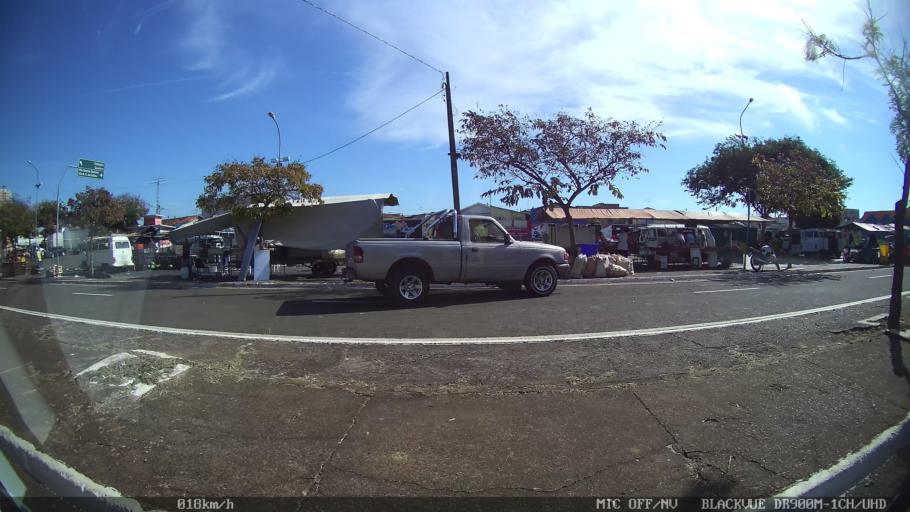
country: BR
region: Sao Paulo
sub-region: Franca
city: Franca
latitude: -20.5311
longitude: -47.4129
